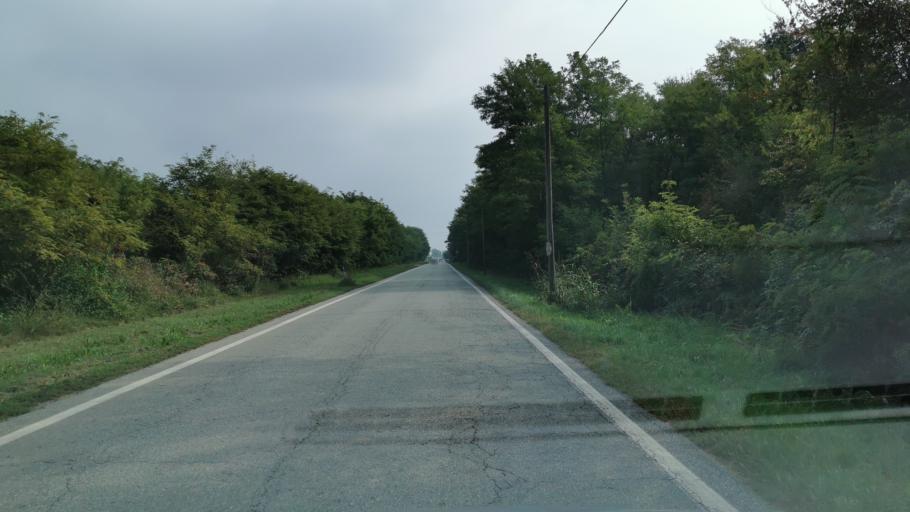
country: IT
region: Piedmont
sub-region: Provincia di Torino
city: Tonengo-Casale
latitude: 45.2651
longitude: 7.9200
